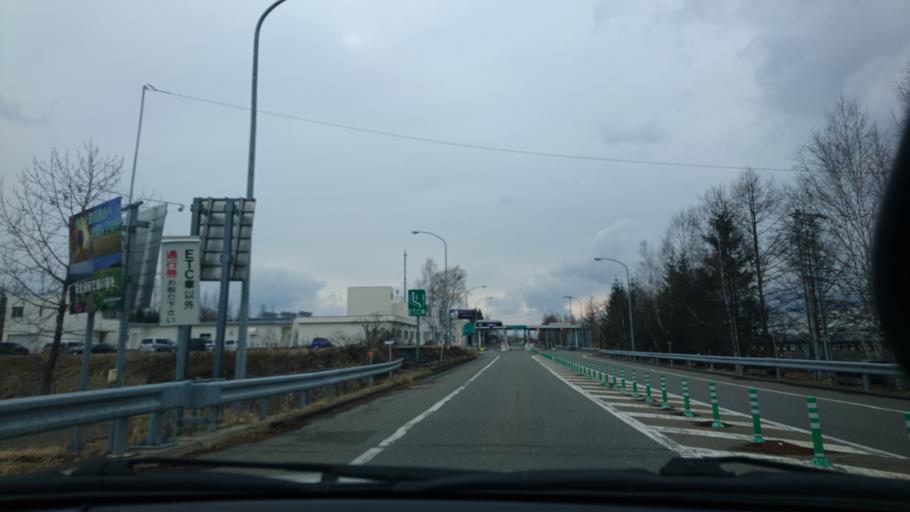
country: JP
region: Hokkaido
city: Otofuke
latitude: 42.9822
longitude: 143.1835
